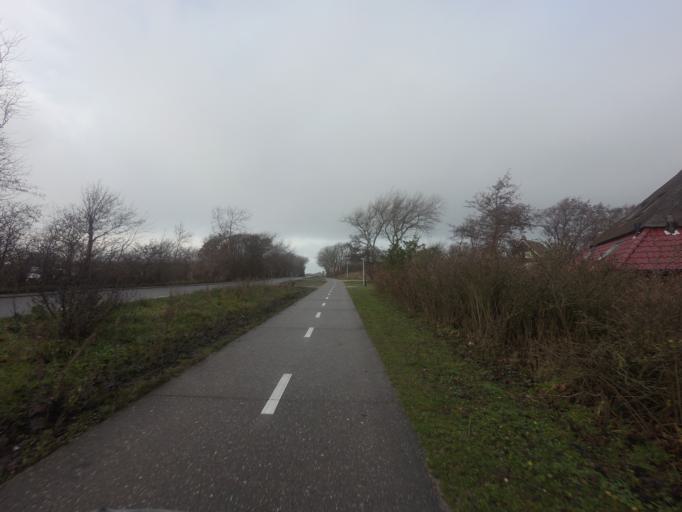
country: NL
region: North Holland
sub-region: Gemeente Texel
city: Den Burg
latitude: 53.1569
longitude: 4.8448
